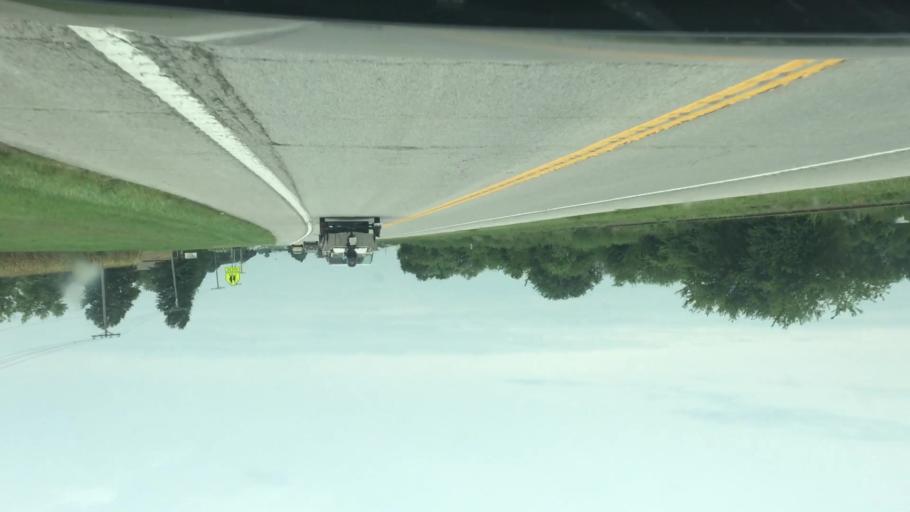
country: US
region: Missouri
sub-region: Pettis County
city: Sedalia
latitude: 38.6945
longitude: -93.1405
